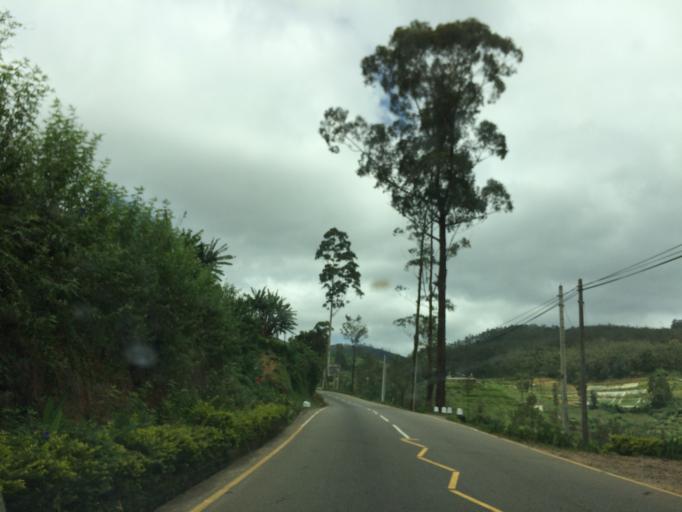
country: LK
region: Central
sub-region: Nuwara Eliya District
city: Nuwara Eliya
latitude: 7.0236
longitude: 80.7213
